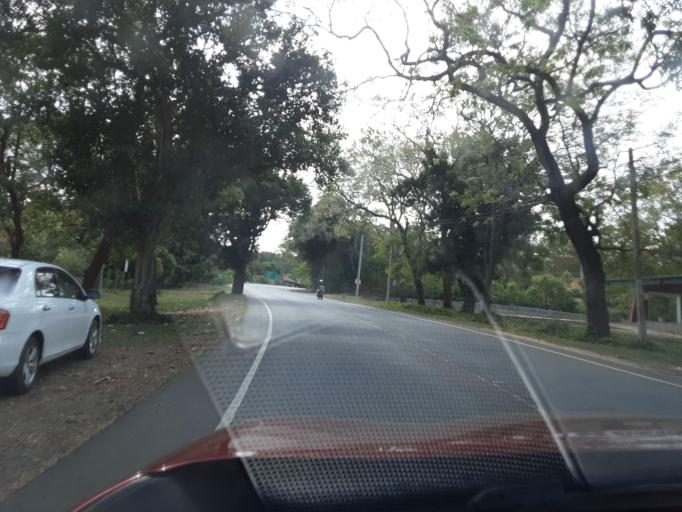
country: LK
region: Uva
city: Haputale
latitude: 6.3459
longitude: 81.1997
